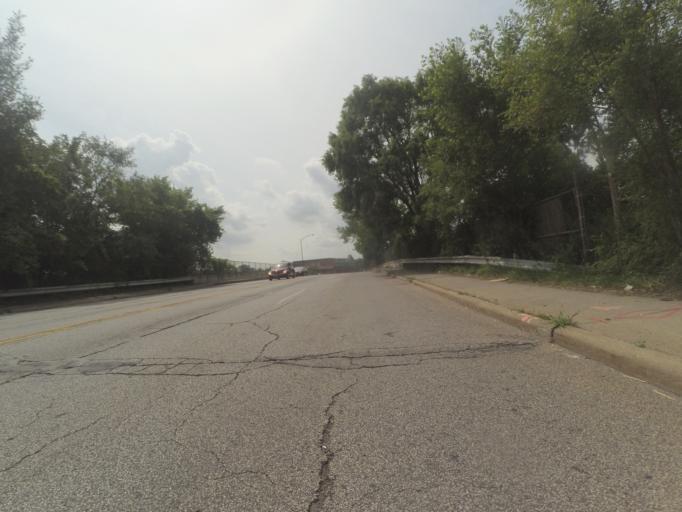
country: US
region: Ohio
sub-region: Cuyahoga County
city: Cleveland
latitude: 41.4766
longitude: -81.7084
